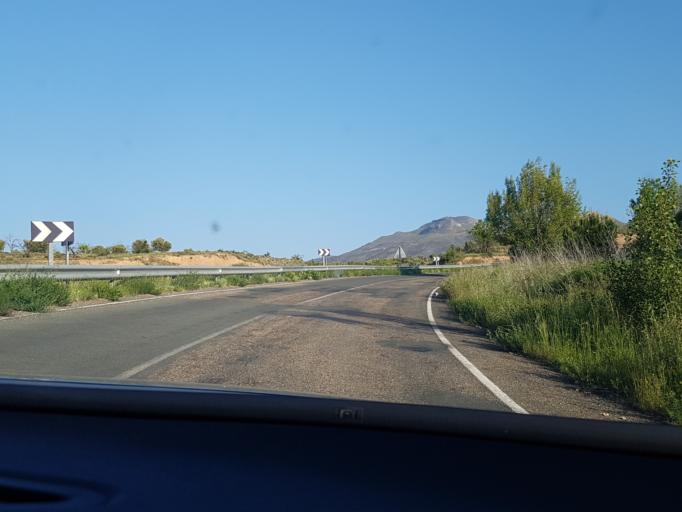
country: ES
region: La Rioja
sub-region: Provincia de La Rioja
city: Santa Eulalia Bajera
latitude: 42.2051
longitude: -2.1873
